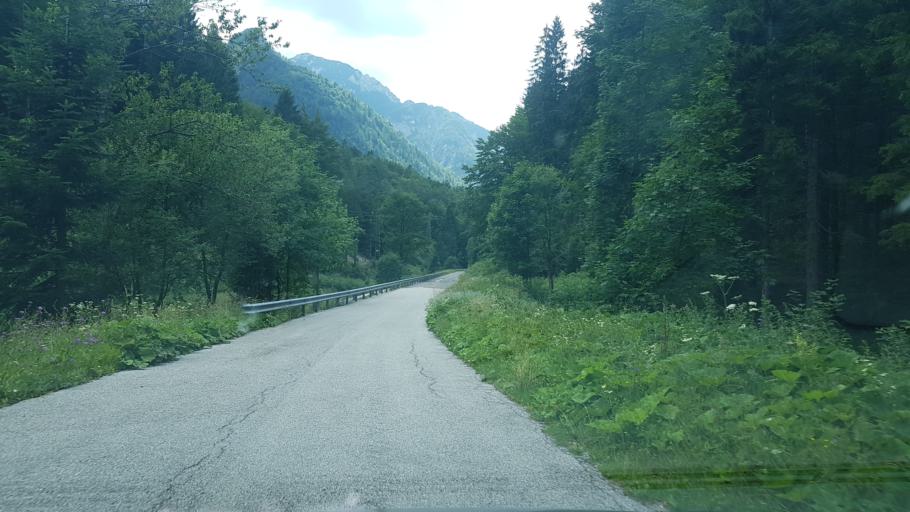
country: IT
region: Friuli Venezia Giulia
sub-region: Provincia di Udine
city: Pontebba
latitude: 46.5021
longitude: 13.2382
